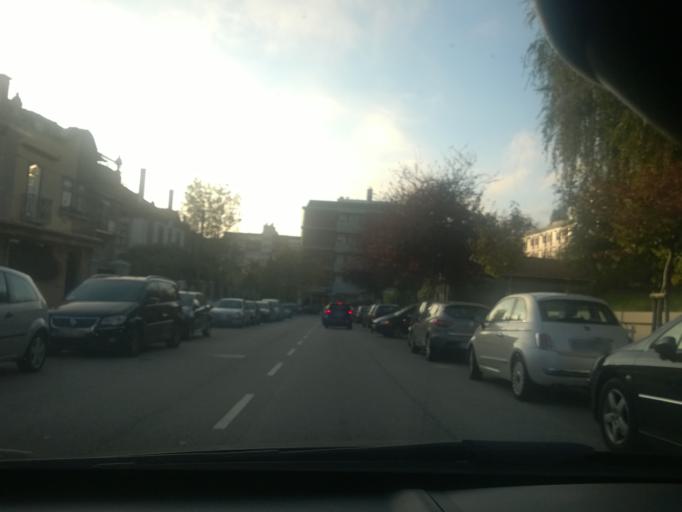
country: PT
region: Porto
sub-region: Matosinhos
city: Senhora da Hora
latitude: 41.1586
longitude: -8.6402
